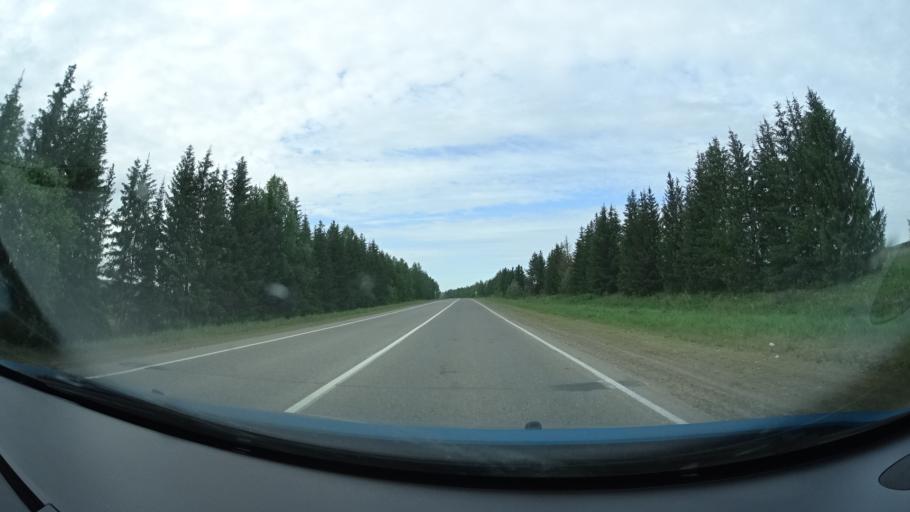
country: RU
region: Perm
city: Barda
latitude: 56.8762
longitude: 55.5982
